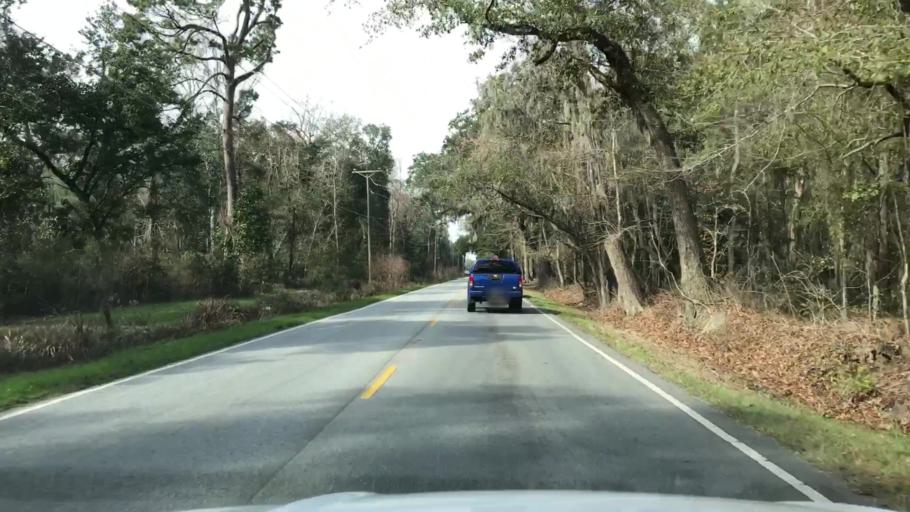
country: US
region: South Carolina
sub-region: Charleston County
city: Shell Point
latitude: 32.7748
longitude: -80.0870
